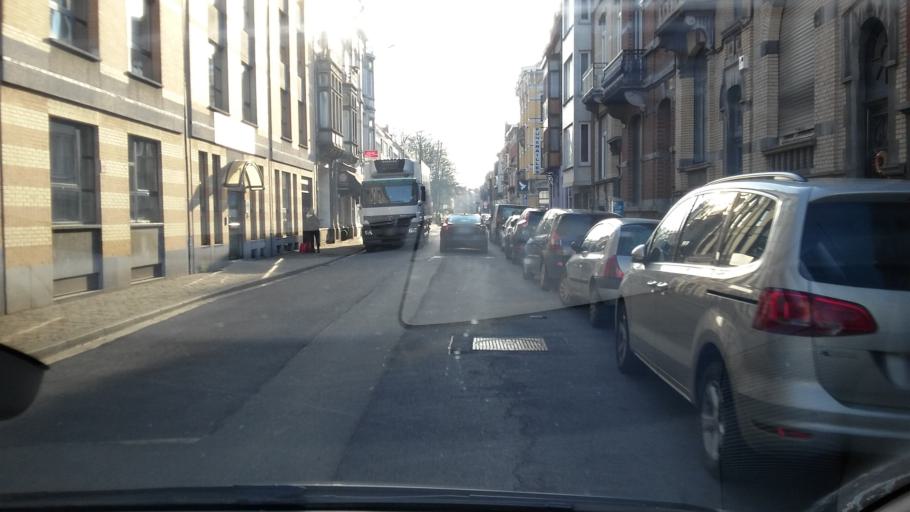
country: BE
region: Brussels Capital
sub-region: Bruxelles-Capitale
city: Brussels
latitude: 50.8457
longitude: 4.3981
